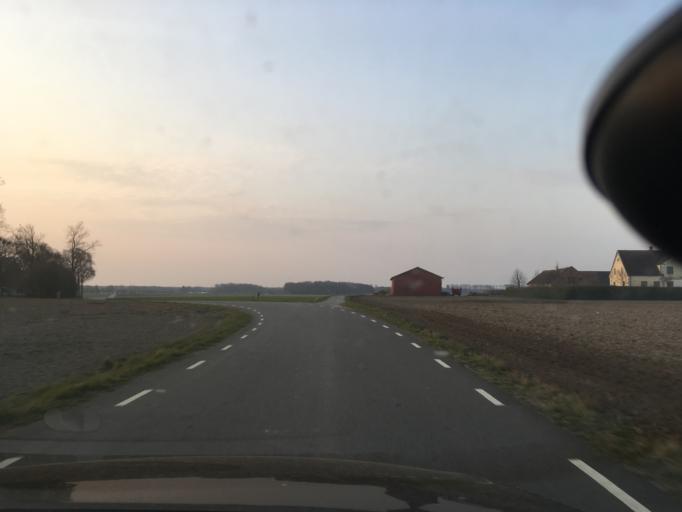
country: SE
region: Skane
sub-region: Ystads Kommun
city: Kopingebro
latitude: 55.4102
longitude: 14.1532
